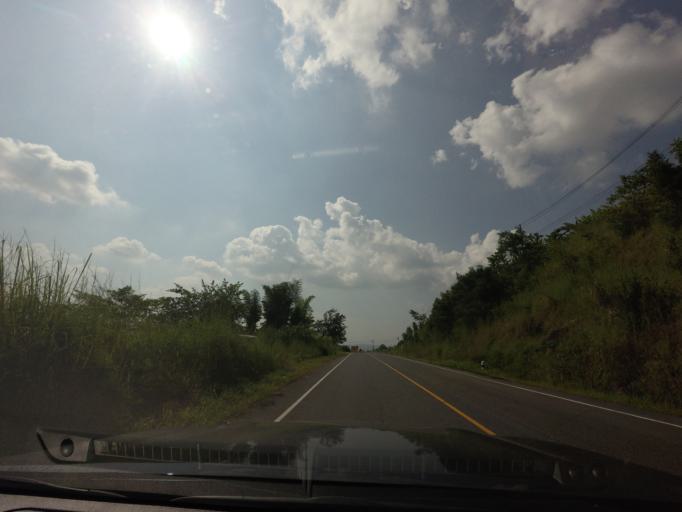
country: TH
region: Nan
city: Santi Suk
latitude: 18.9815
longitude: 100.9650
